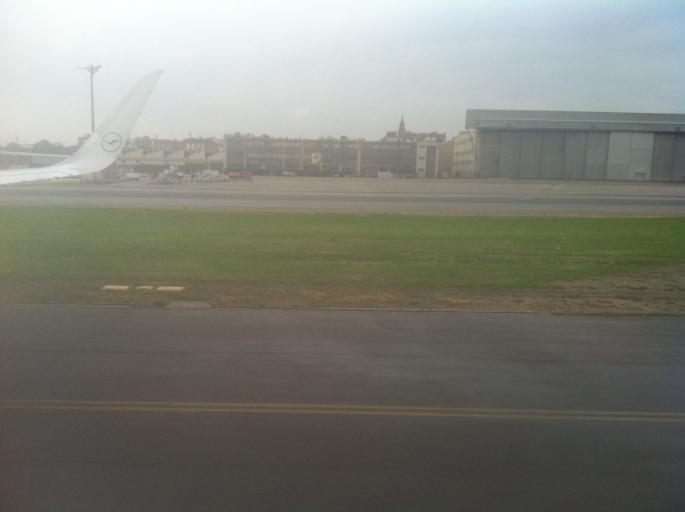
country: ES
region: Madrid
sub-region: Provincia de Madrid
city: Barajas de Madrid
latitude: 40.4777
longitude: -3.5714
